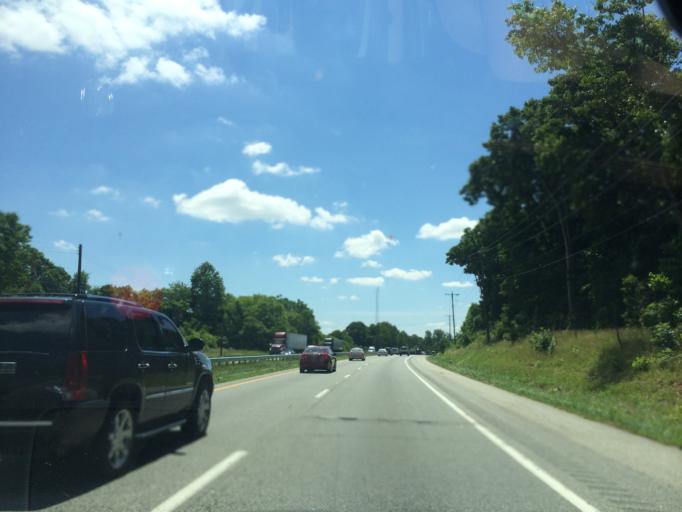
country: US
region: Maryland
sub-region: Queen Anne's County
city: Centreville
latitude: 38.9499
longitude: -76.0671
